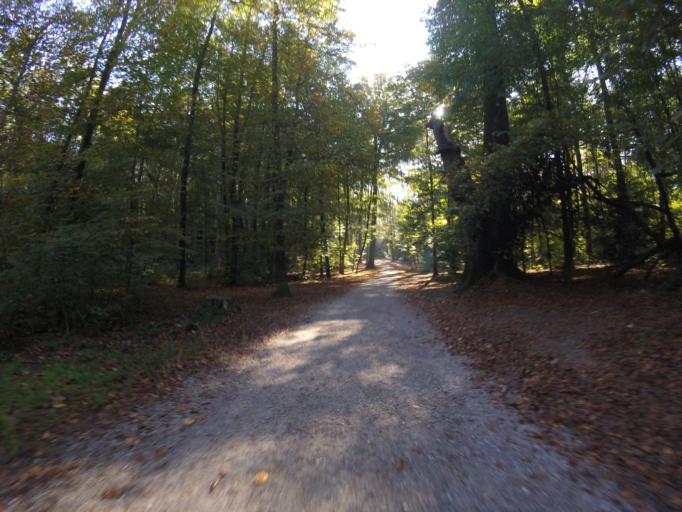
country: CH
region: Bern
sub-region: Bern-Mittelland District
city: Bern
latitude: 46.9386
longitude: 7.4551
